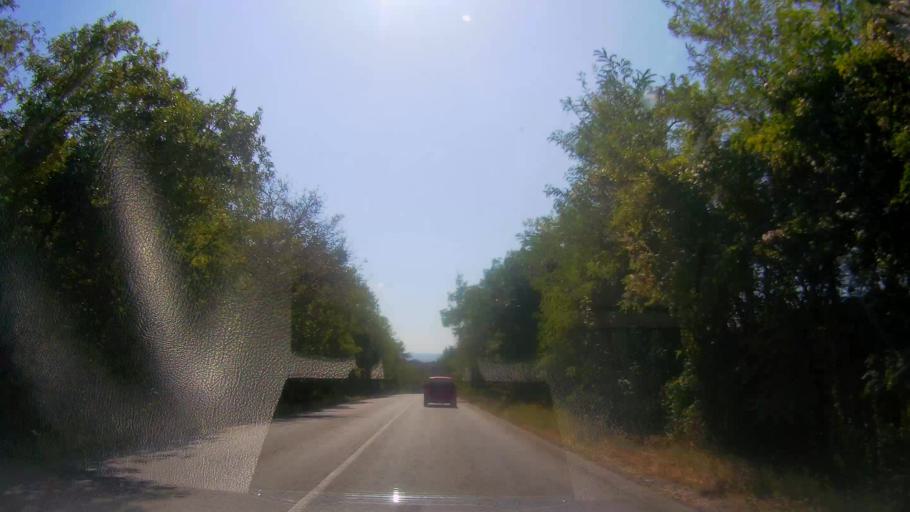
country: BG
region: Veliko Turnovo
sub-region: Obshtina Gorna Oryakhovitsa
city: Purvomaytsi
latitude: 43.2530
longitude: 25.6432
